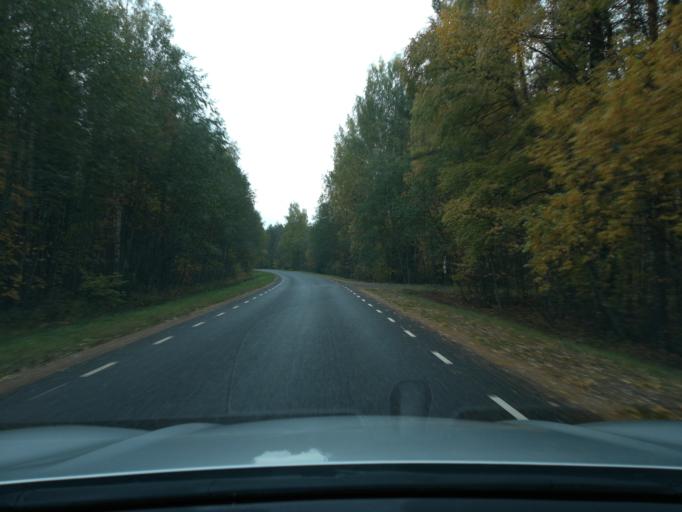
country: EE
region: Ida-Virumaa
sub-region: Johvi vald
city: Johvi
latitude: 59.0294
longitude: 27.3912
